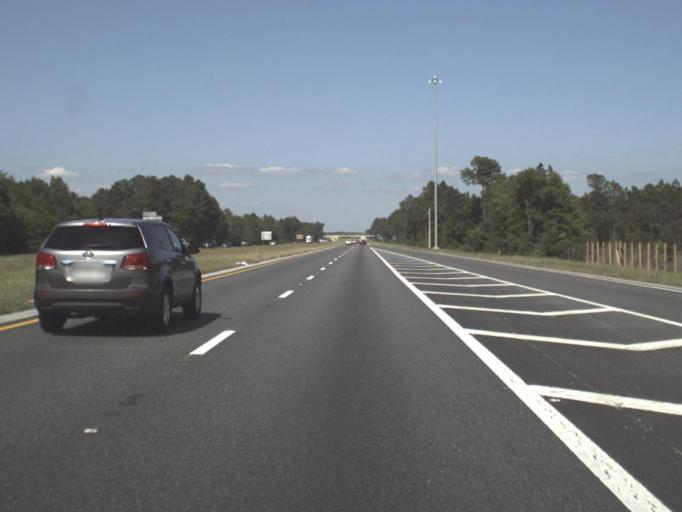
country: US
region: Florida
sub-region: Santa Rosa County
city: Bagdad
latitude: 30.5723
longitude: -87.0281
